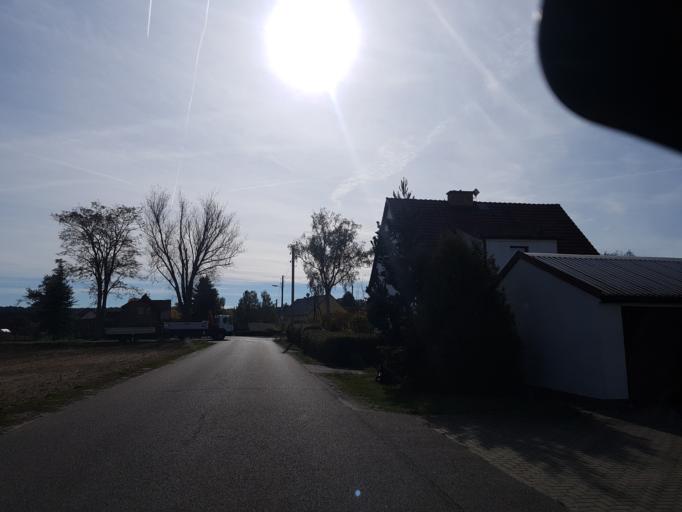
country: DE
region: Brandenburg
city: Schlieben
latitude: 51.7597
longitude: 13.3521
